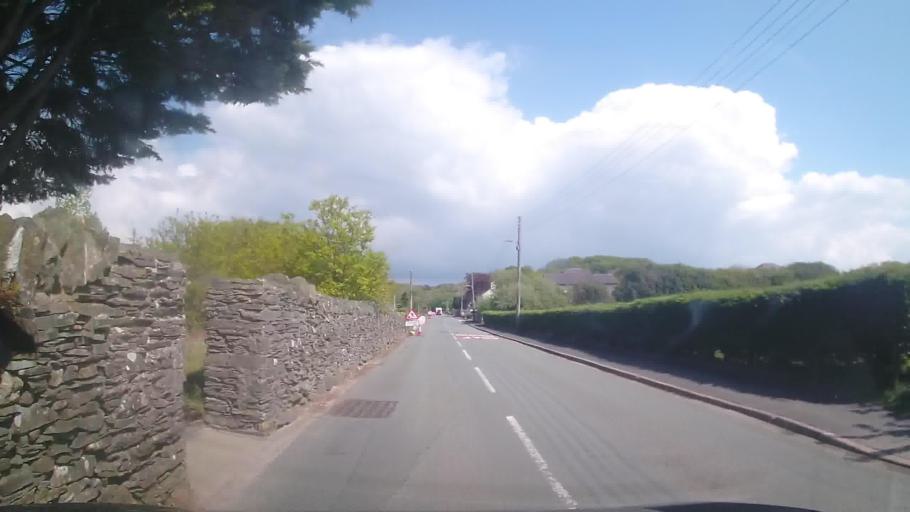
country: GB
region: Wales
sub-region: Gwynedd
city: Porthmadog
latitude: 52.9141
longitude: -4.1603
